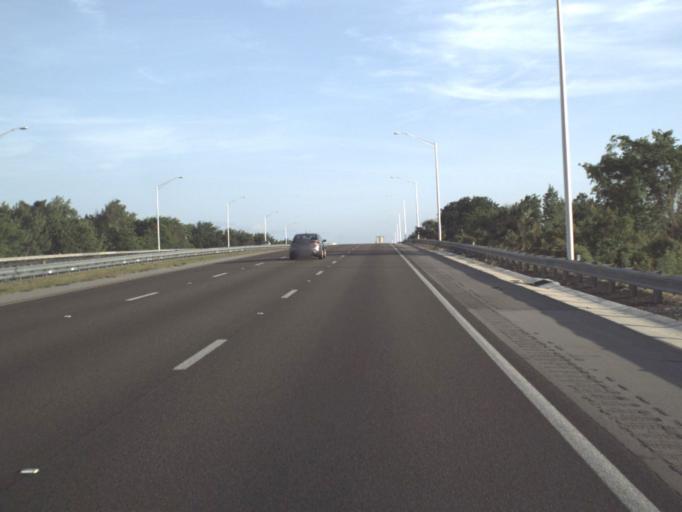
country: US
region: Florida
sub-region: Volusia County
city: Oak Hill
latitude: 28.7739
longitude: -80.8948
